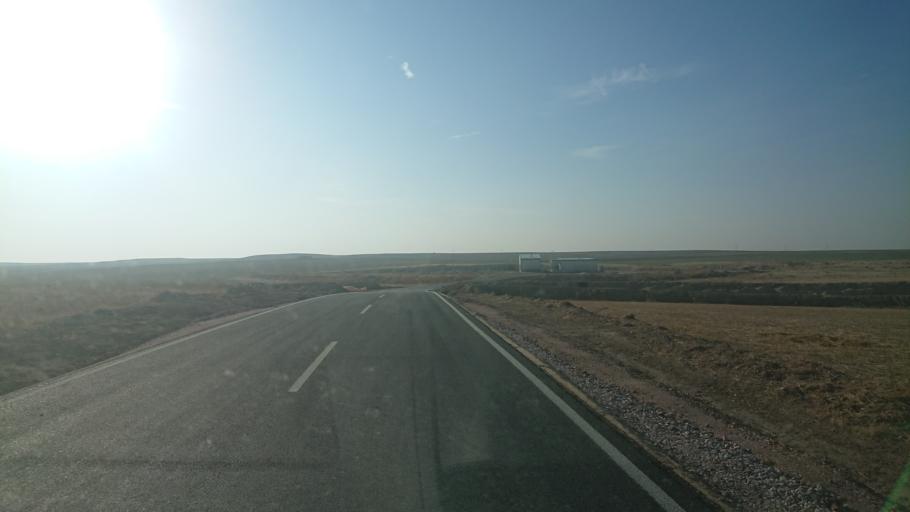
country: TR
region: Aksaray
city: Sultanhani
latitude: 38.0843
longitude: 33.6136
